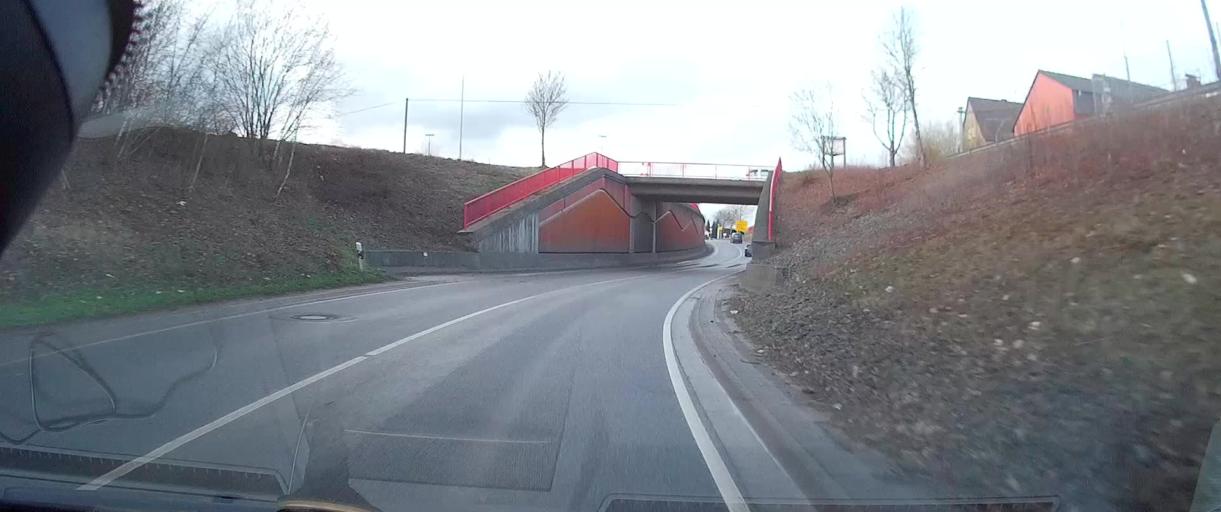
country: DE
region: Rheinland-Pfalz
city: Mogendorf
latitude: 50.4835
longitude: 7.7727
